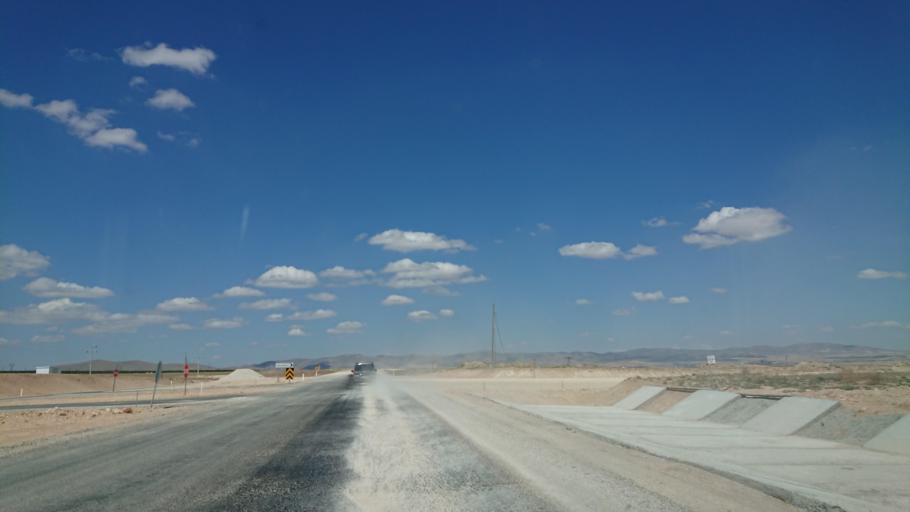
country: TR
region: Kirsehir
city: Kirsehir
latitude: 39.1318
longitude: 34.0419
